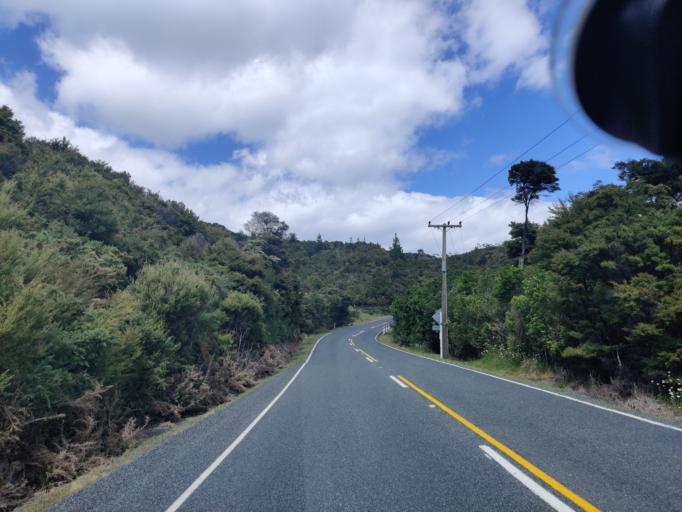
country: NZ
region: Northland
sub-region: Far North District
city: Paihia
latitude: -35.2593
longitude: 174.2246
